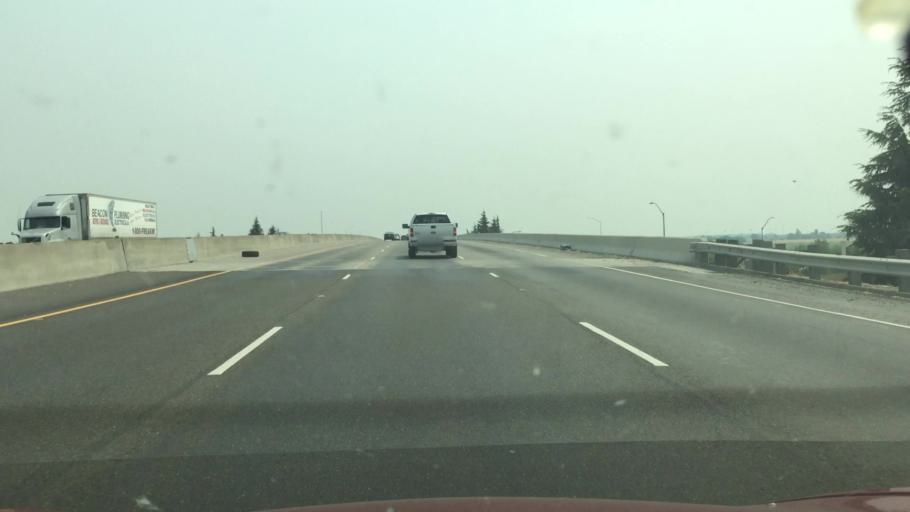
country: US
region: California
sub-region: San Joaquin County
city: Kennedy
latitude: 37.9057
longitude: -121.2233
